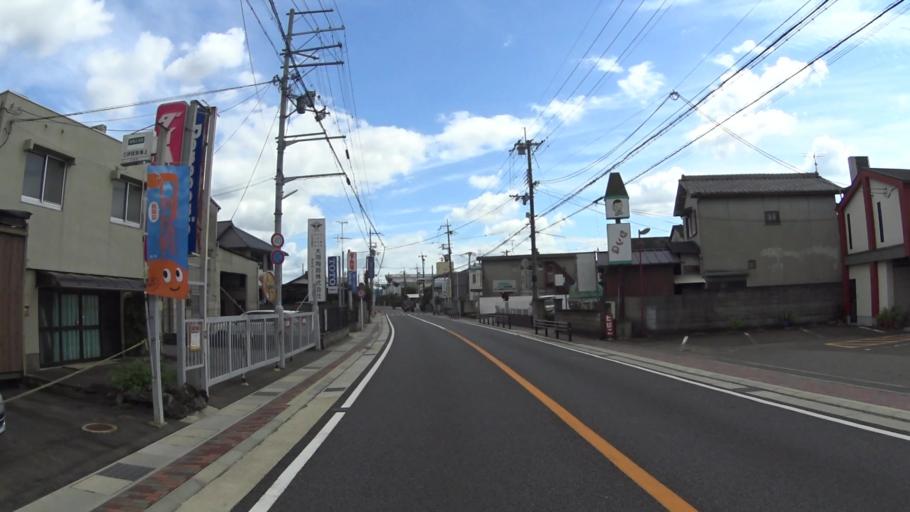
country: JP
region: Kyoto
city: Yawata
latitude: 34.8880
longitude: 135.7224
